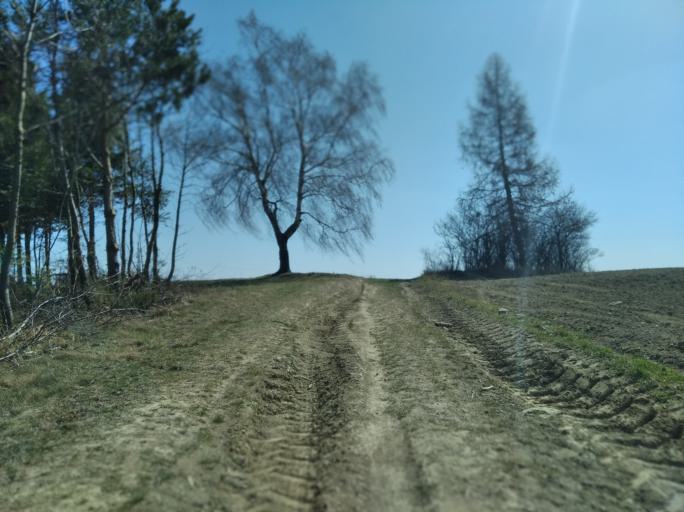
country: PL
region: Subcarpathian Voivodeship
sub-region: Powiat strzyzowski
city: Polomia
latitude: 49.8789
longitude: 21.8596
